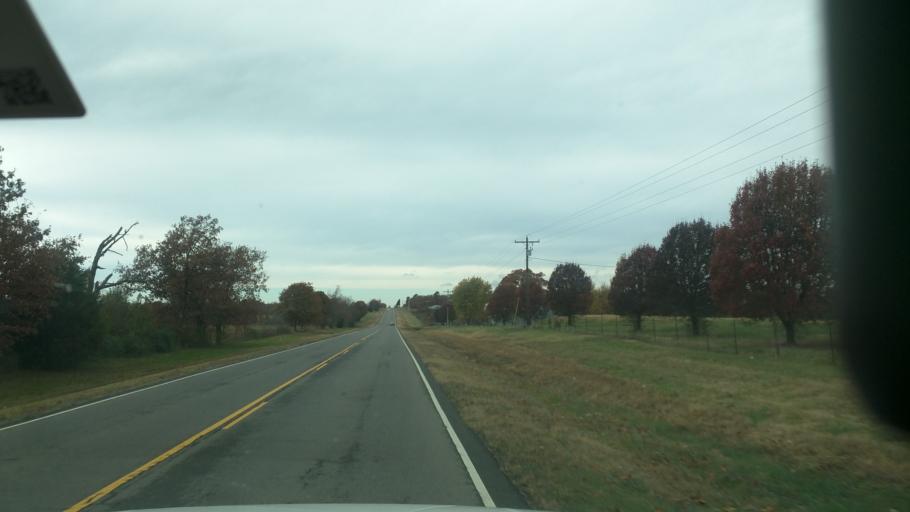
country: US
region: Oklahoma
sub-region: Cherokee County
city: Park Hill
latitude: 35.8974
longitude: -94.7915
